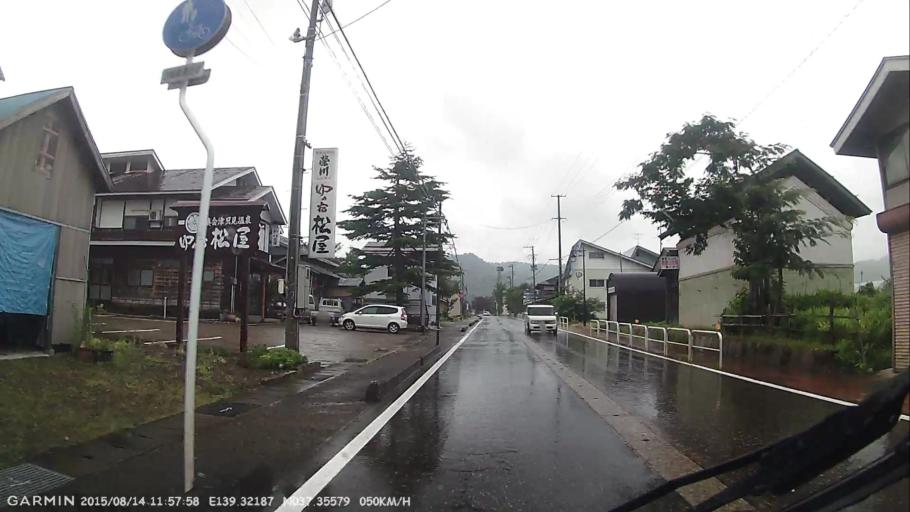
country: JP
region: Niigata
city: Muramatsu
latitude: 37.3958
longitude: 139.4081
